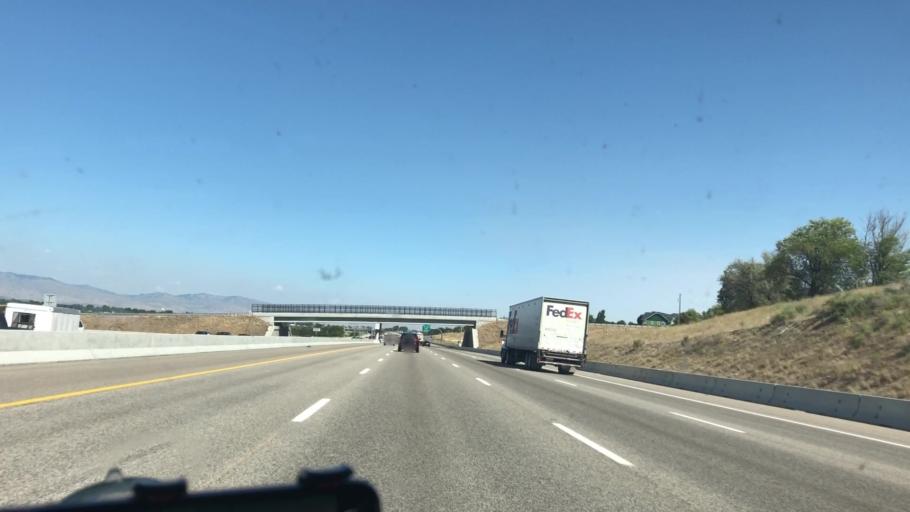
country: US
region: Idaho
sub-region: Ada County
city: Meridian
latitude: 43.5951
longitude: -116.4568
